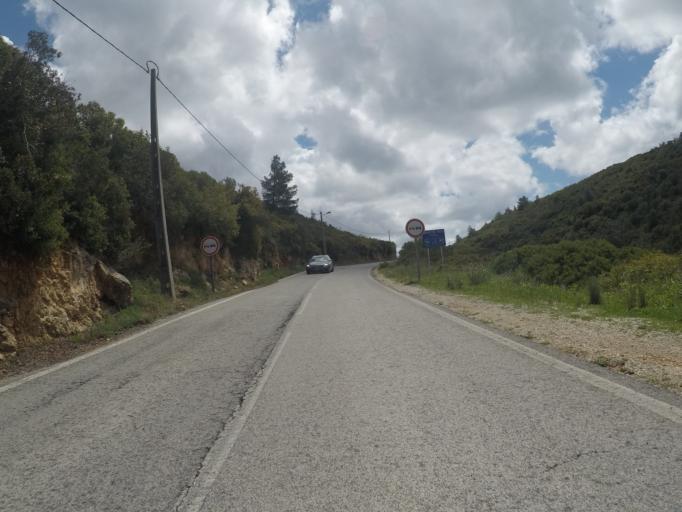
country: PT
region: Faro
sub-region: Vila do Bispo
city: Vila do Bispo
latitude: 37.0708
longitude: -8.8267
